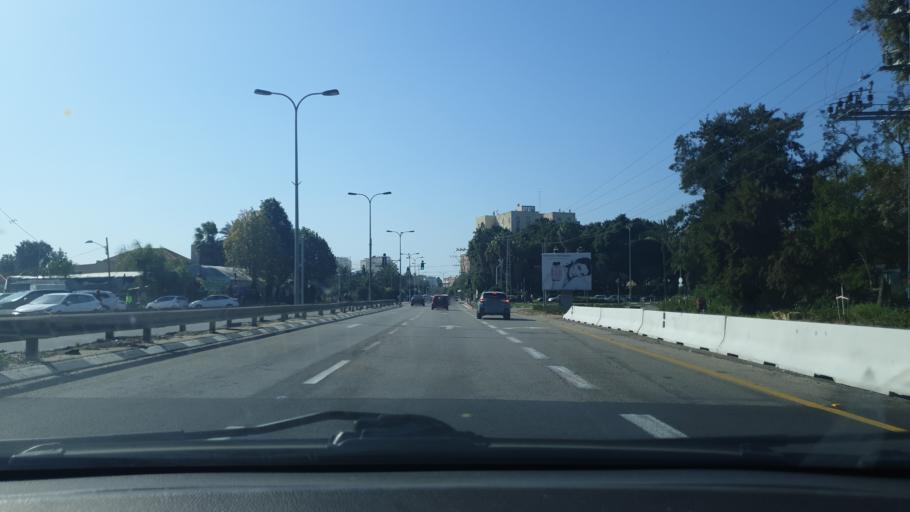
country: IL
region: Tel Aviv
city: Azor
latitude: 32.0444
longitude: 34.8145
